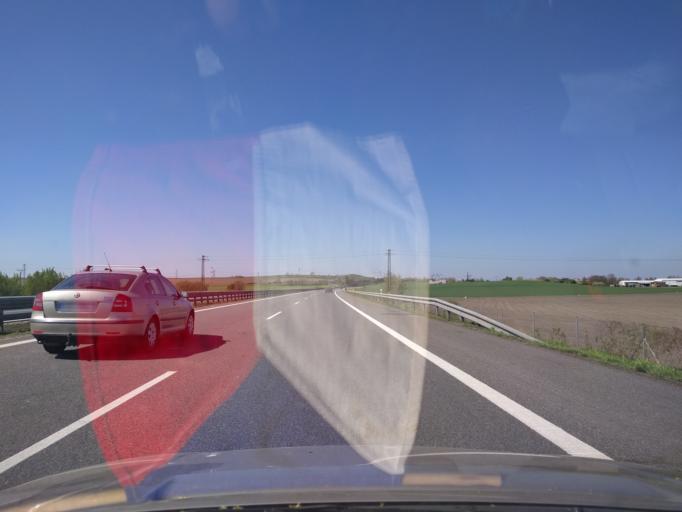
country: CZ
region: Central Bohemia
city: Prerov nad Labem
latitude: 50.1345
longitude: 14.8164
